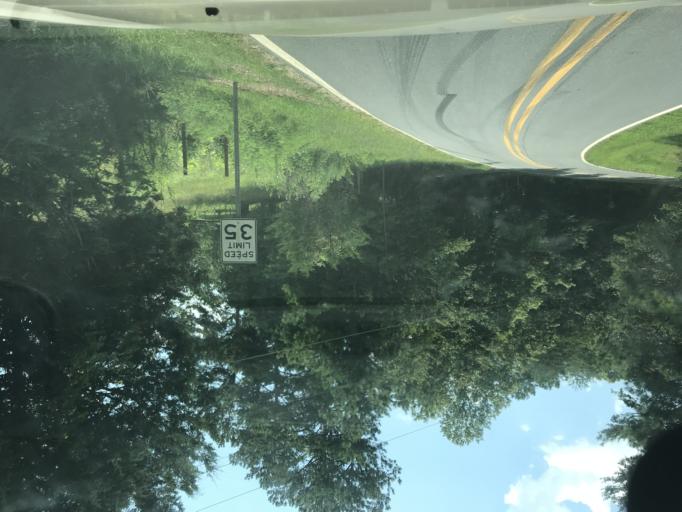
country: US
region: Georgia
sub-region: Forsyth County
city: Cumming
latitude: 34.3118
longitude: -84.2036
